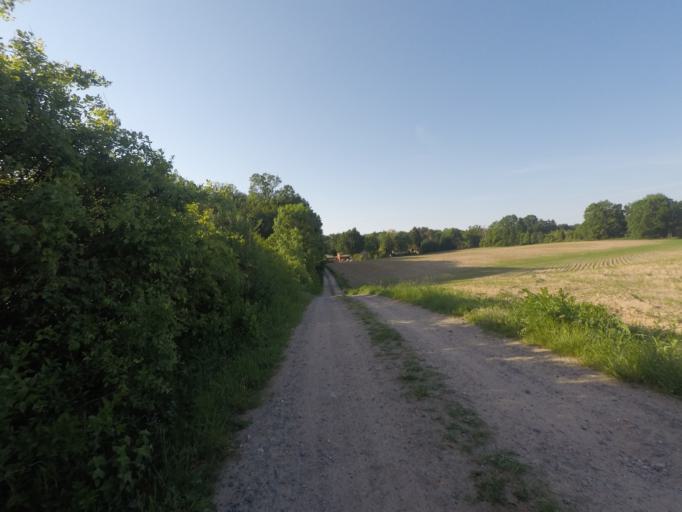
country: DE
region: Brandenburg
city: Joachimsthal
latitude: 52.9031
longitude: 13.7022
